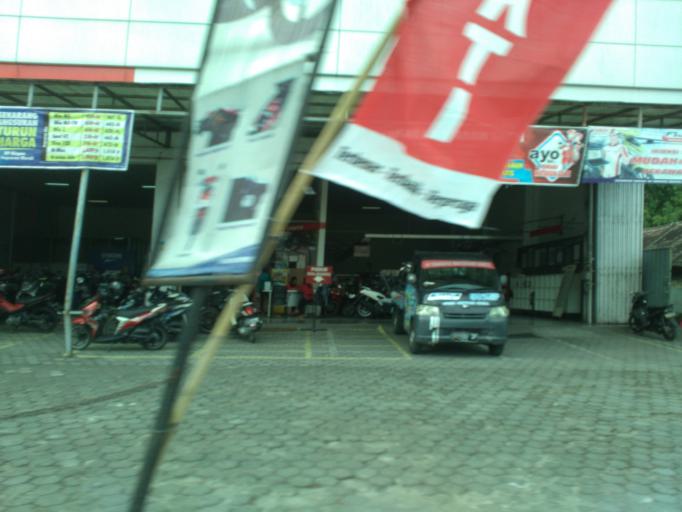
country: ID
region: Central Java
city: Trucuk
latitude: -7.6851
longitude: 110.6436
